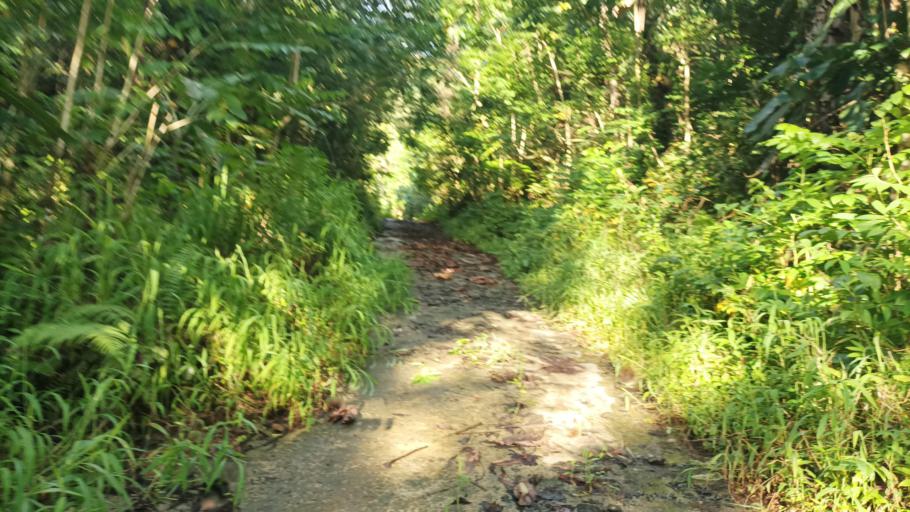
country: FM
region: Pohnpei
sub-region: Kolonia Municipality
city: Kolonia Town
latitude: 6.9625
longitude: 158.1858
